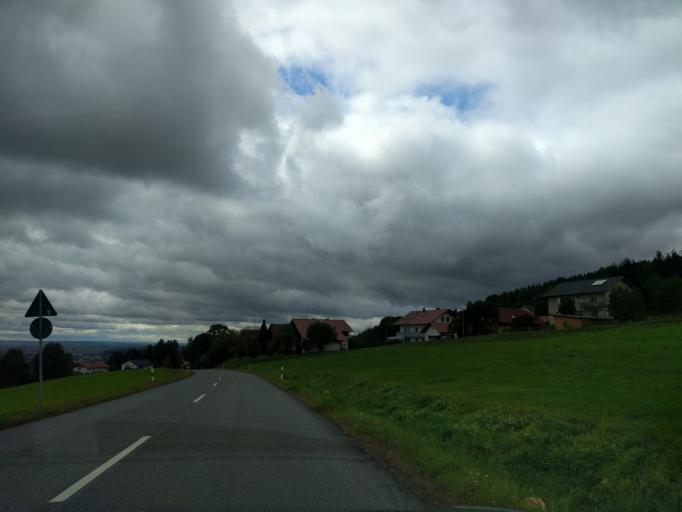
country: DE
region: Bavaria
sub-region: Lower Bavaria
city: Deggendorf
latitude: 48.8336
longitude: 12.9998
